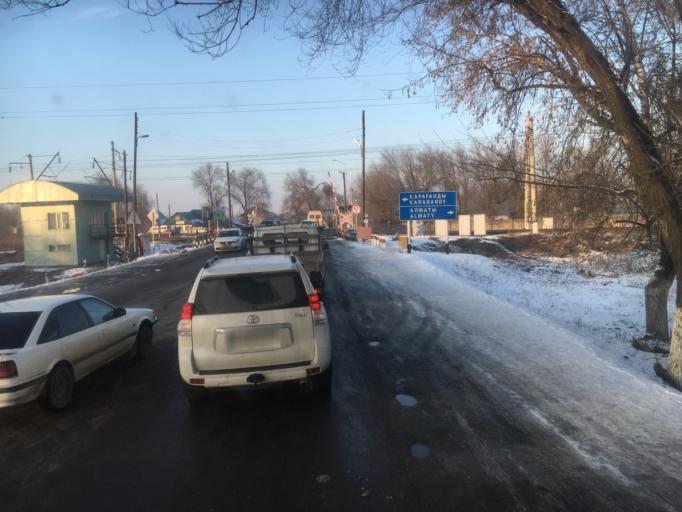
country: KZ
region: Almaty Oblysy
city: Burunday
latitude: 43.3761
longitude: 76.6420
